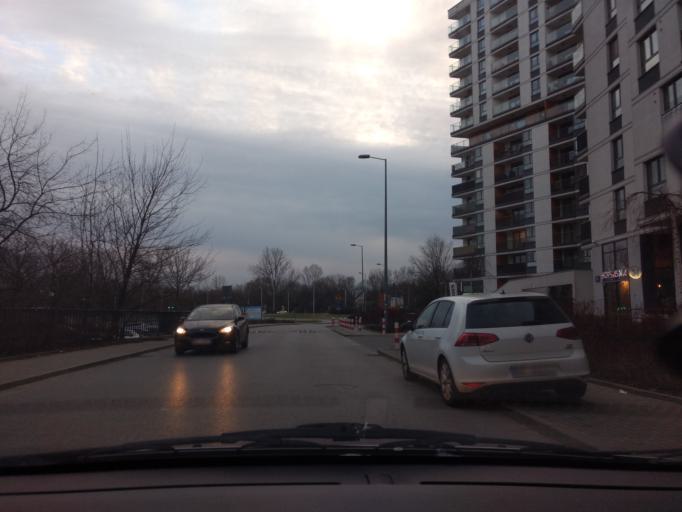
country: PL
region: Masovian Voivodeship
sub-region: Warszawa
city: Praga Poludnie
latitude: 52.2279
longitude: 21.0782
